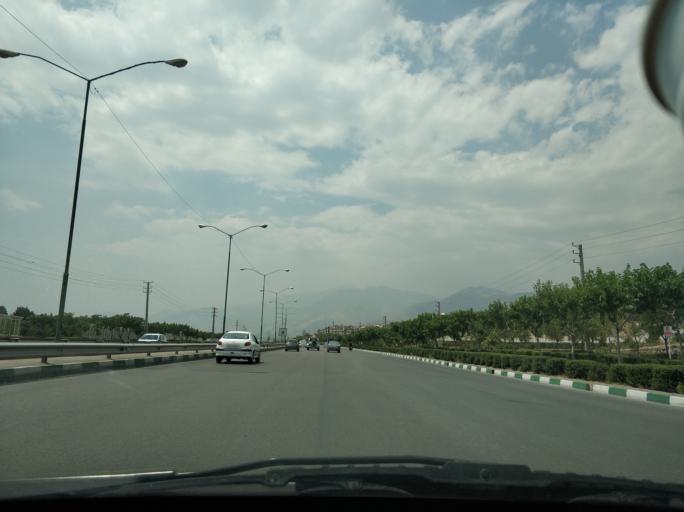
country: IR
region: Tehran
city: Tajrish
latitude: 35.7630
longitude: 51.5686
